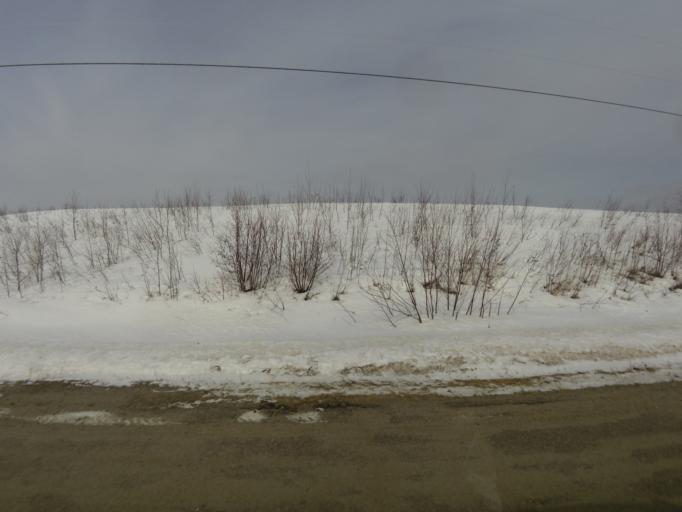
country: CA
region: Quebec
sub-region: Laurentides
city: Ferme-Neuve
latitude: 46.9314
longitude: -75.3281
